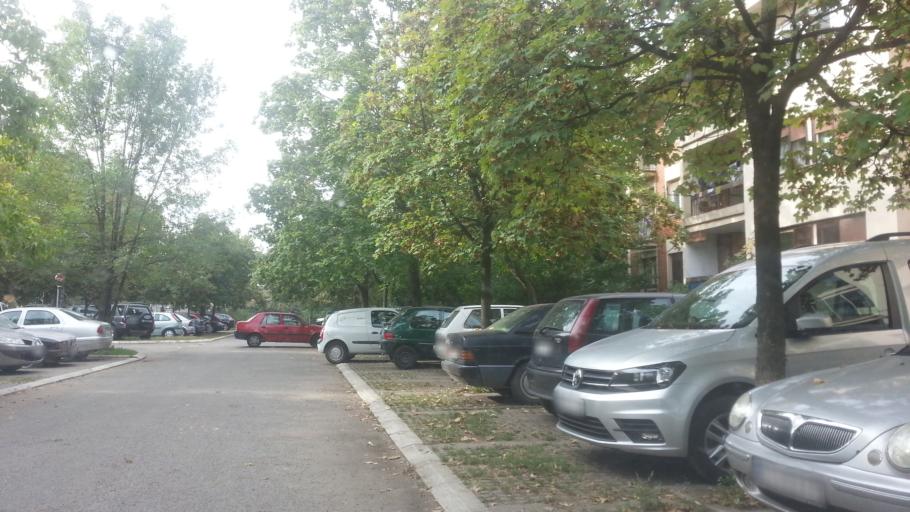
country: RS
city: Novi Banovci
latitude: 44.9667
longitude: 20.2802
